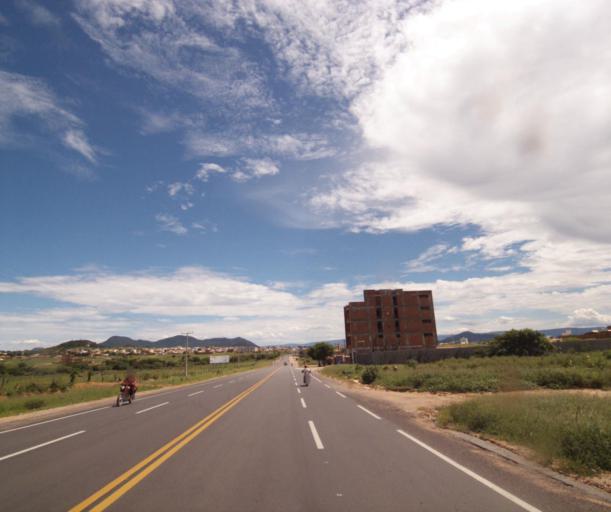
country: BR
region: Bahia
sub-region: Guanambi
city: Guanambi
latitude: -14.2181
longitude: -42.7618
